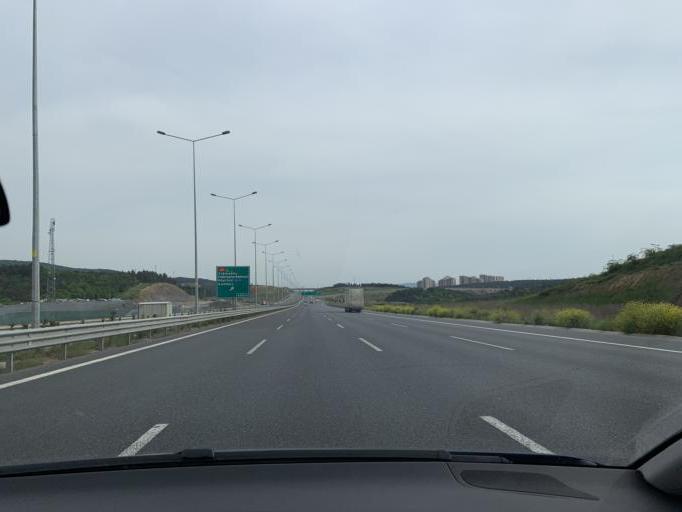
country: TR
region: Istanbul
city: Sancaktepe
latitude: 41.0616
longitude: 29.2755
